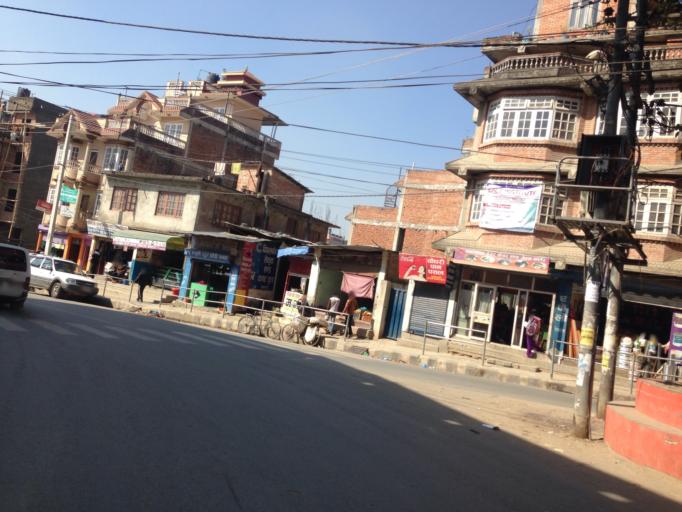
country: NP
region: Central Region
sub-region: Bagmati Zone
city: Kathmandu
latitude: 27.7242
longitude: 85.3397
